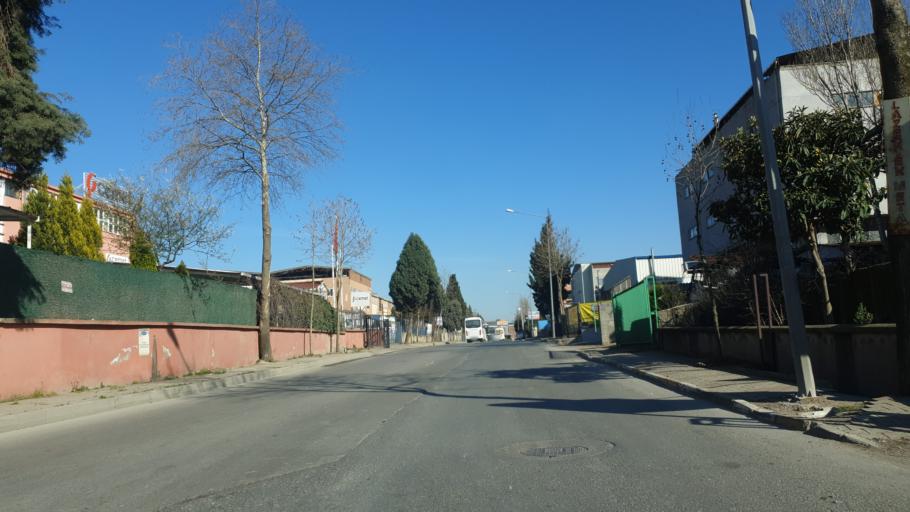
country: TR
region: Istanbul
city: Icmeler
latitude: 40.8784
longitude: 29.3610
